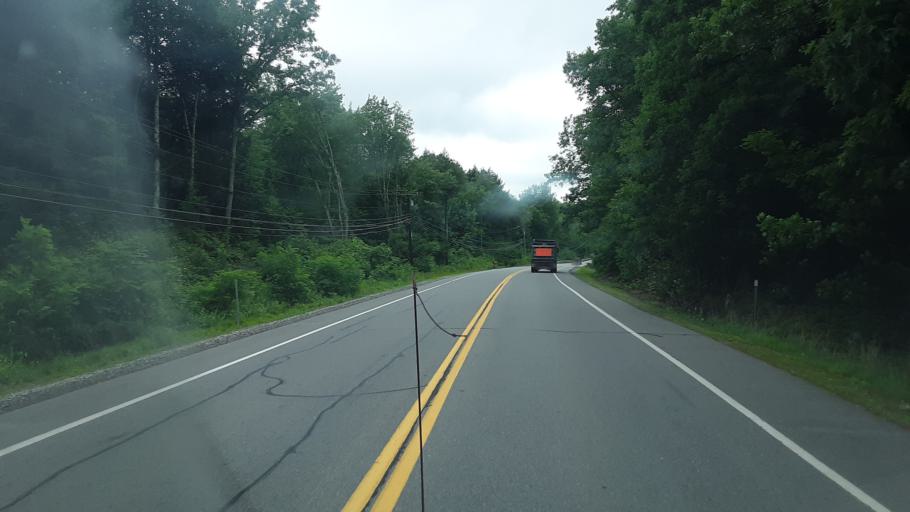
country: US
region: New Hampshire
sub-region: Rockingham County
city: Nottingham
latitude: 43.1583
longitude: -71.0702
